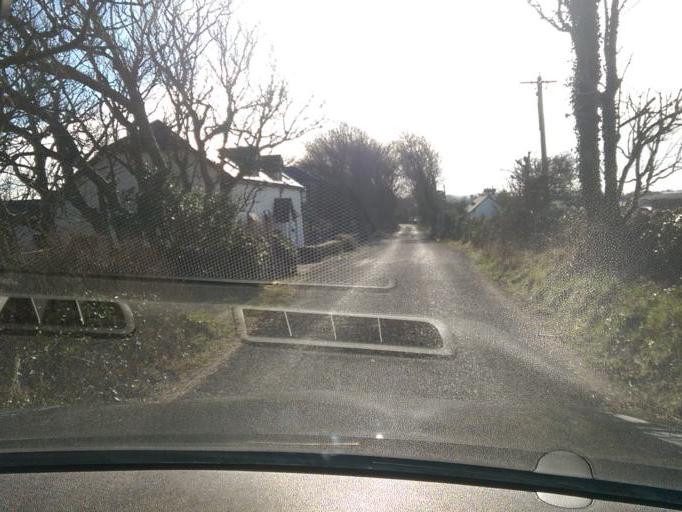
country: IE
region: Connaught
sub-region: County Galway
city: Oranmore
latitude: 53.2434
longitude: -8.9585
